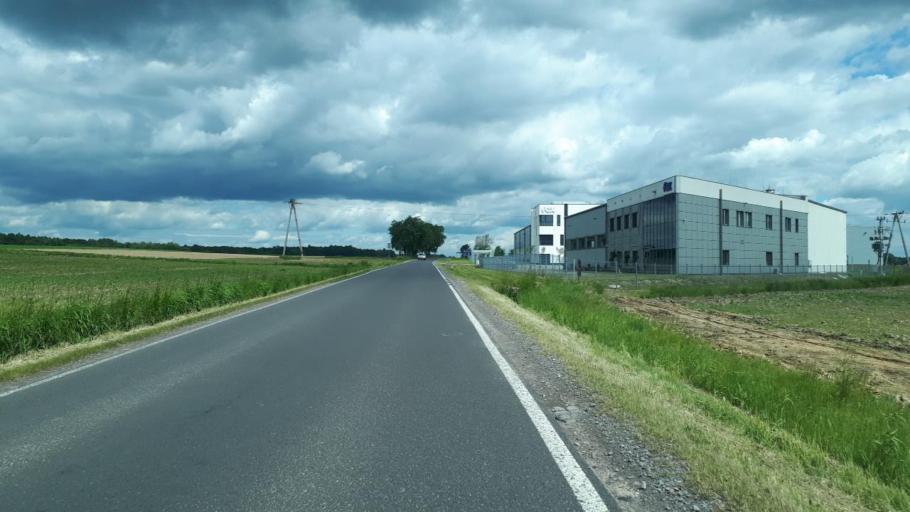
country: PL
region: Silesian Voivodeship
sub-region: Powiat bielski
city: Wilamowice
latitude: 49.9282
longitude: 19.1497
